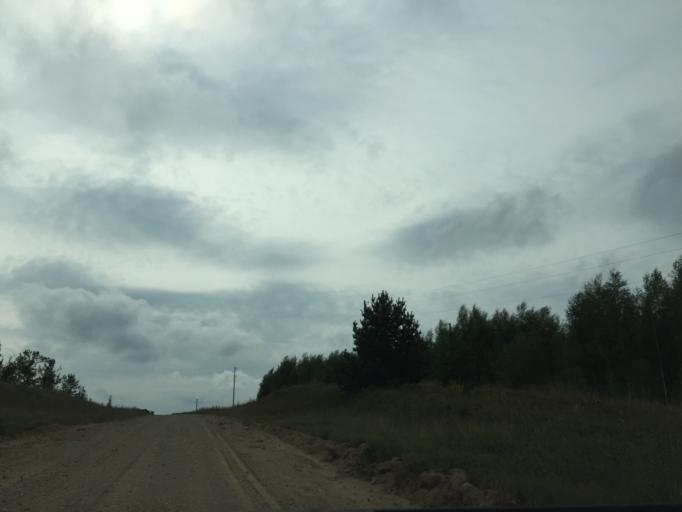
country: LV
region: Dagda
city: Dagda
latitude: 56.2440
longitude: 27.7929
